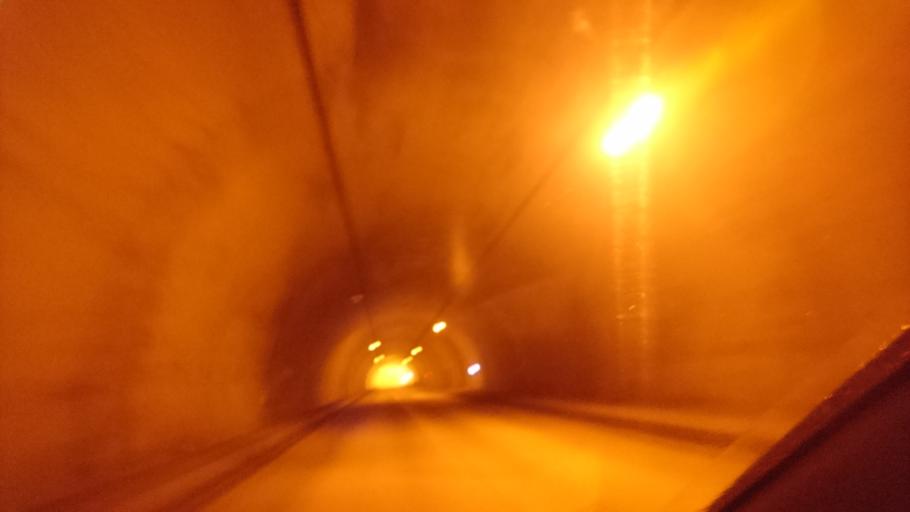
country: JP
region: Iwate
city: Mizusawa
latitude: 39.1227
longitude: 140.9066
